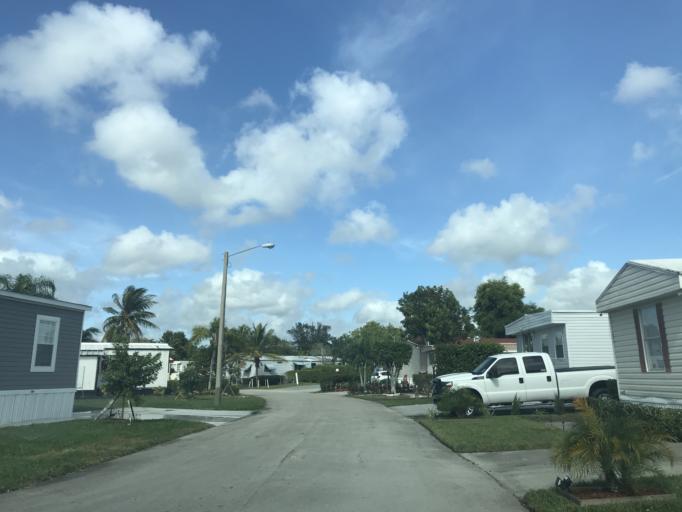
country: US
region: Florida
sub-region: Palm Beach County
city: Boca Pointe
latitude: 26.3100
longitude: -80.1747
